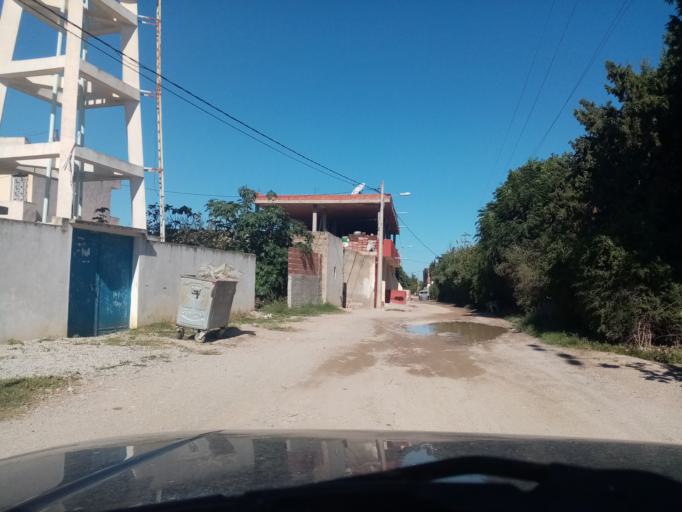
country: TN
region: Nabul
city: Bu `Urqub
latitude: 36.5745
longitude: 10.5731
